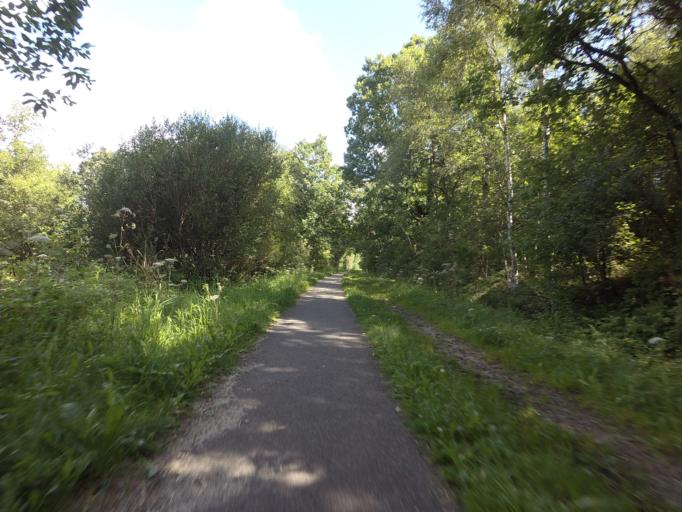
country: DK
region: Central Jutland
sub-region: Silkeborg Kommune
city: Svejbaek
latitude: 56.2155
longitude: 9.7076
